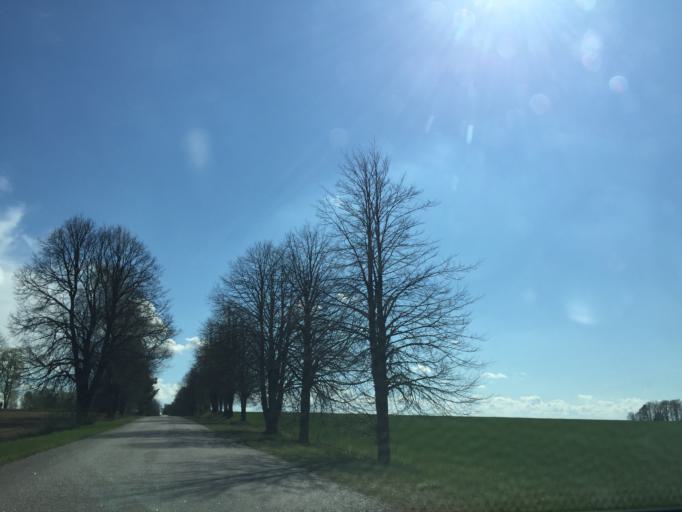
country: LV
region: Strenci
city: Strenci
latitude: 57.5566
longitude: 25.7128
